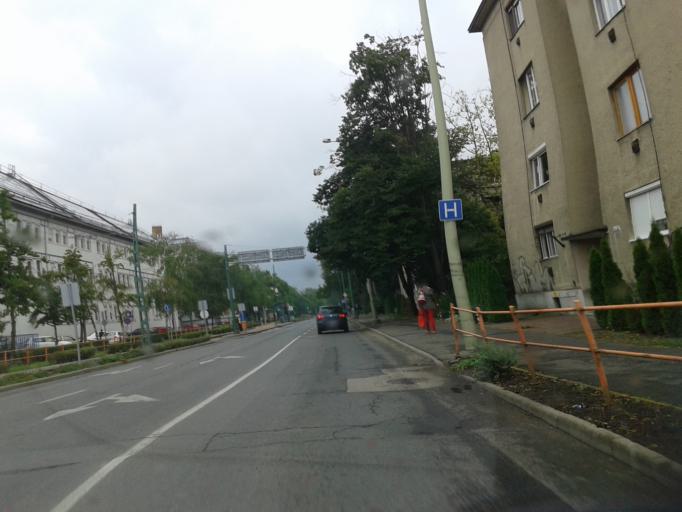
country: HU
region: Csongrad
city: Szeged
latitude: 46.2535
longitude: 20.1243
